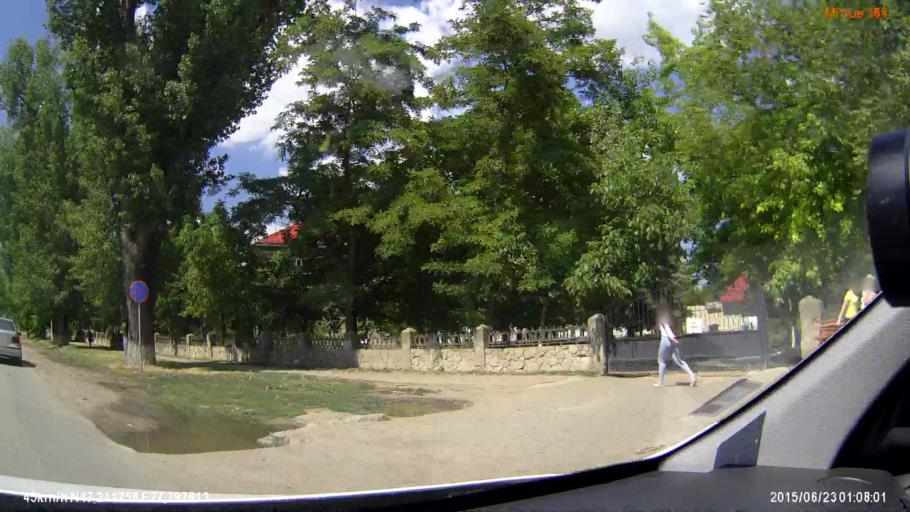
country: MD
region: Ungheni
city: Ungheni
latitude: 47.2123
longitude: 27.7974
